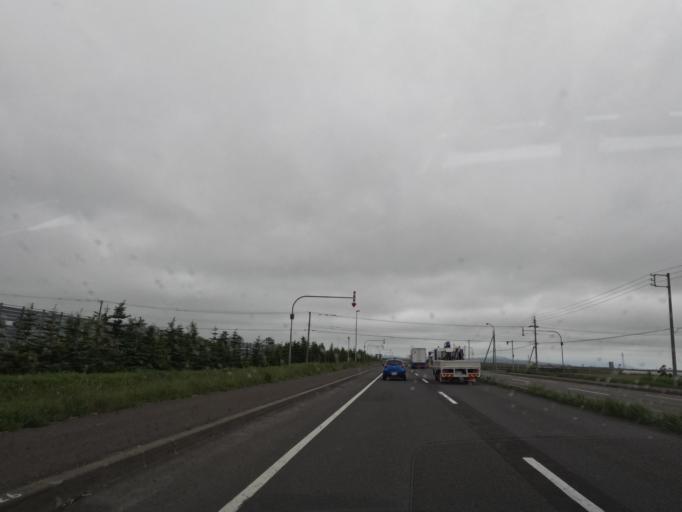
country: JP
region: Hokkaido
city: Tobetsu
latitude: 43.1728
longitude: 141.5216
